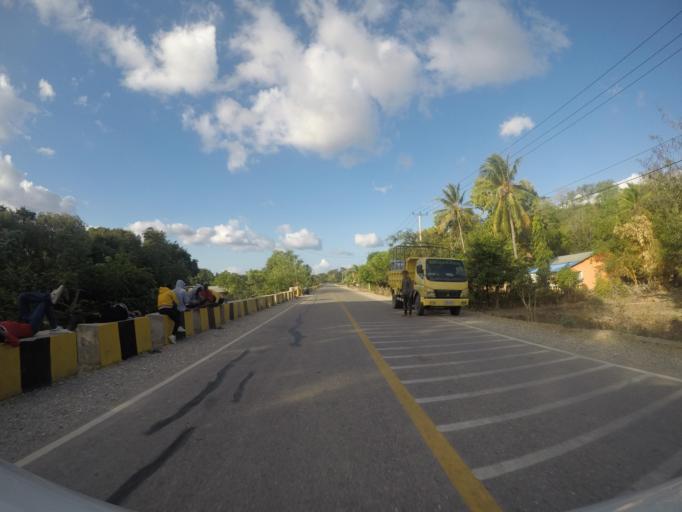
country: TL
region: Lautem
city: Lospalos
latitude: -8.3666
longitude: 126.8979
